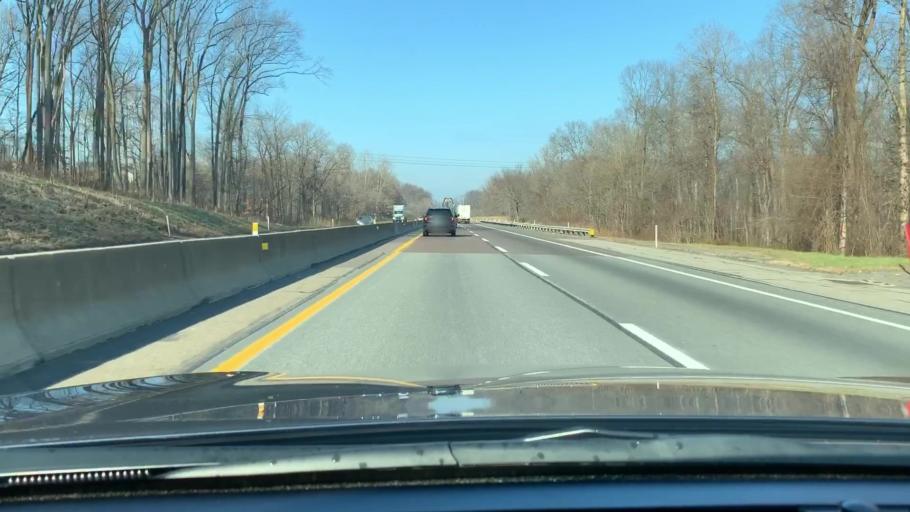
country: US
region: Pennsylvania
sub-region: Chester County
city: Elverson
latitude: 40.1061
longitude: -75.7566
